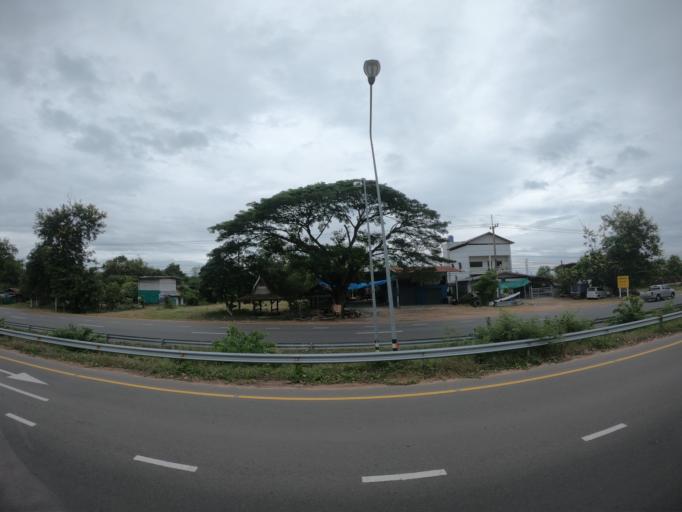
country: TH
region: Roi Et
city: Changhan
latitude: 16.1198
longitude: 103.4866
